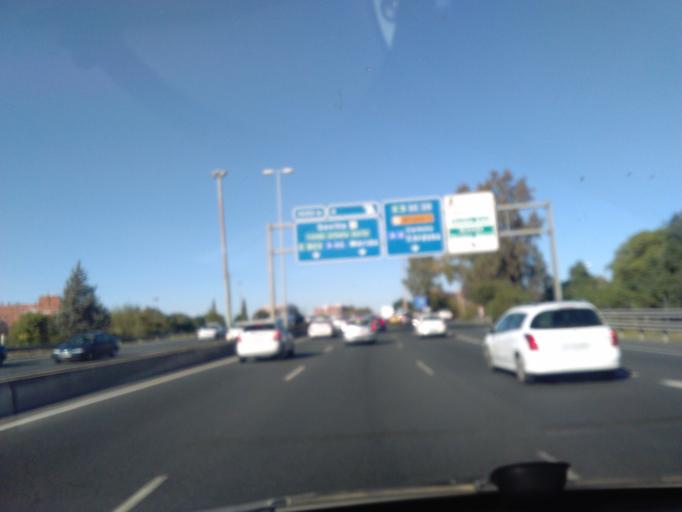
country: ES
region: Andalusia
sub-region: Provincia de Sevilla
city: Sevilla
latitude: 37.3978
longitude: -5.9449
